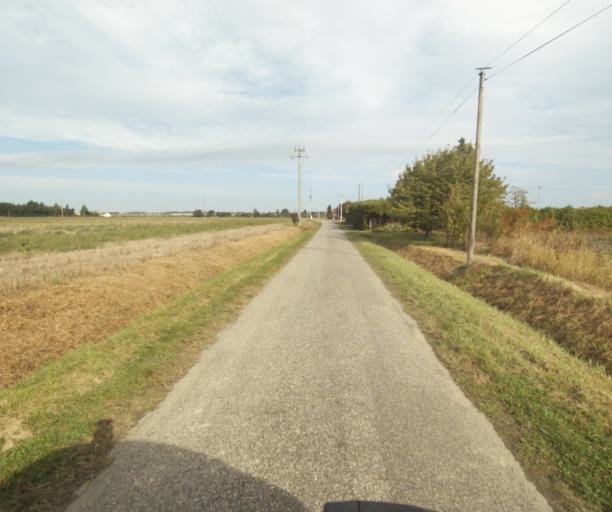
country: FR
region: Midi-Pyrenees
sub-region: Departement du Tarn-et-Garonne
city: Montech
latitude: 43.9383
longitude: 1.2228
